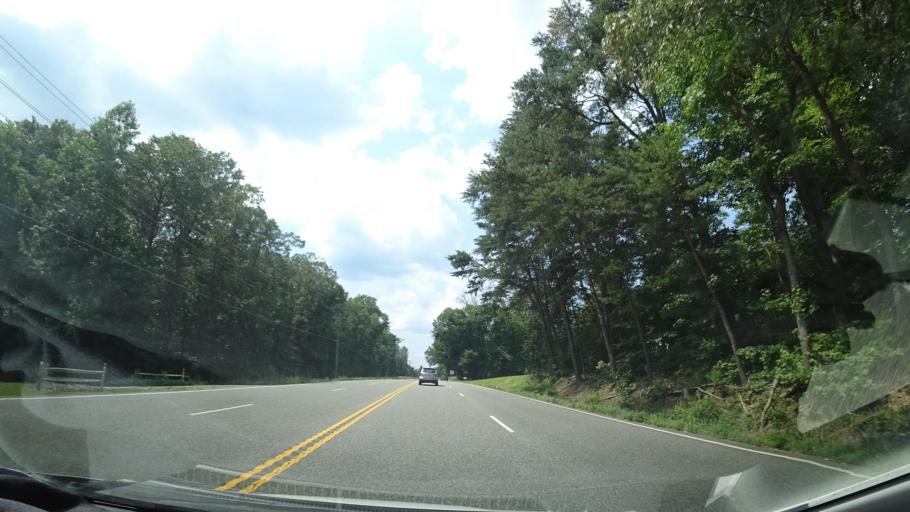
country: US
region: Virginia
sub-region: Hanover County
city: Ashland
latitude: 37.8995
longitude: -77.4691
